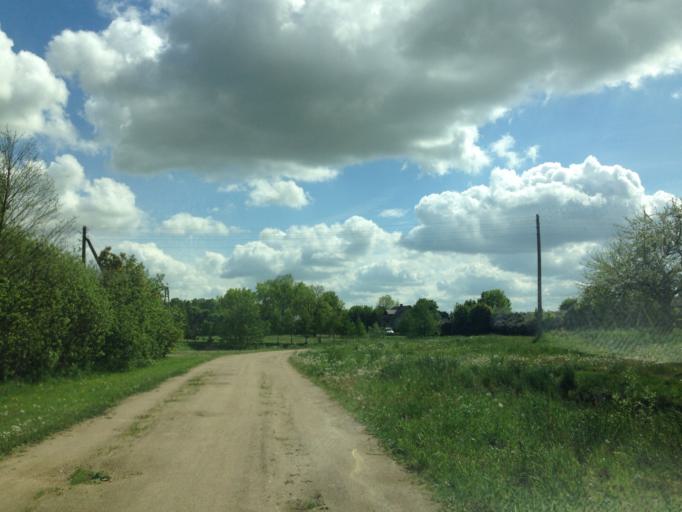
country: PL
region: Warmian-Masurian Voivodeship
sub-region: Powiat ostrodzki
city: Dabrowno
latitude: 53.3949
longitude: 20.1344
